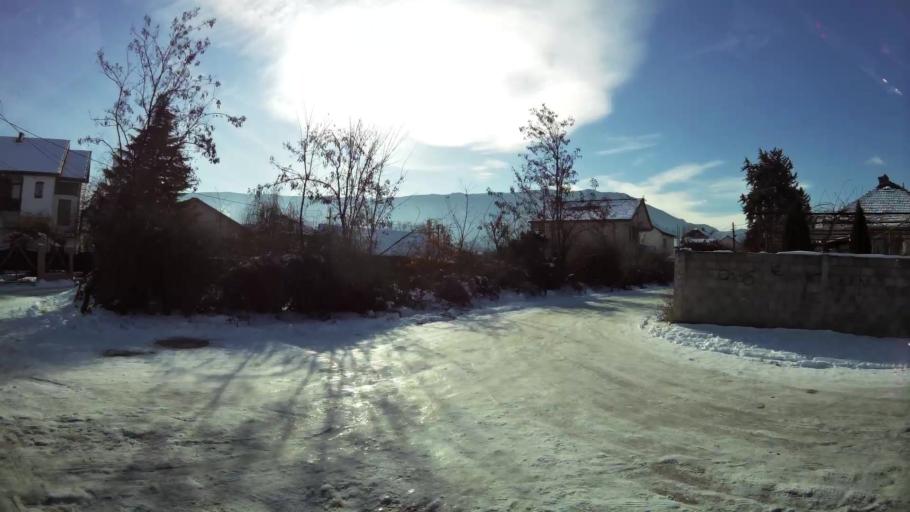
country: MK
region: Saraj
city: Saraj
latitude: 41.9998
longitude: 21.3301
